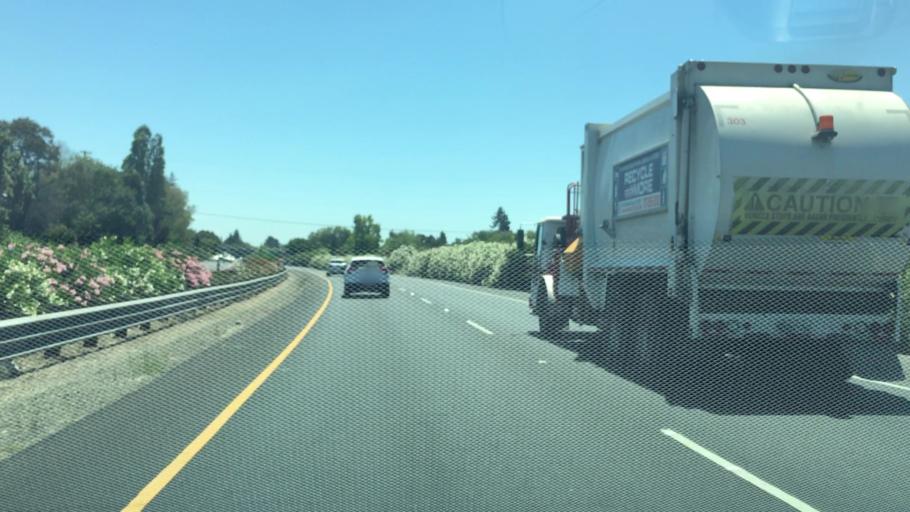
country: US
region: California
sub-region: Napa County
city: Napa
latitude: 38.2922
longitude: -122.3023
